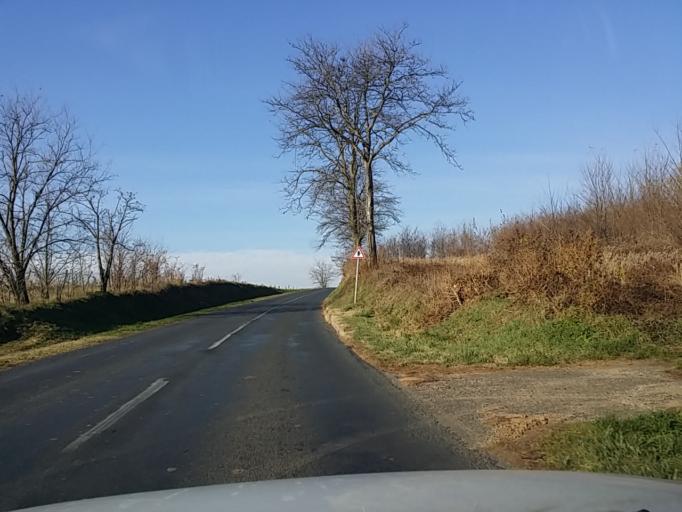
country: HU
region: Veszprem
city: Badacsonytomaj
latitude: 46.8595
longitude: 17.5035
